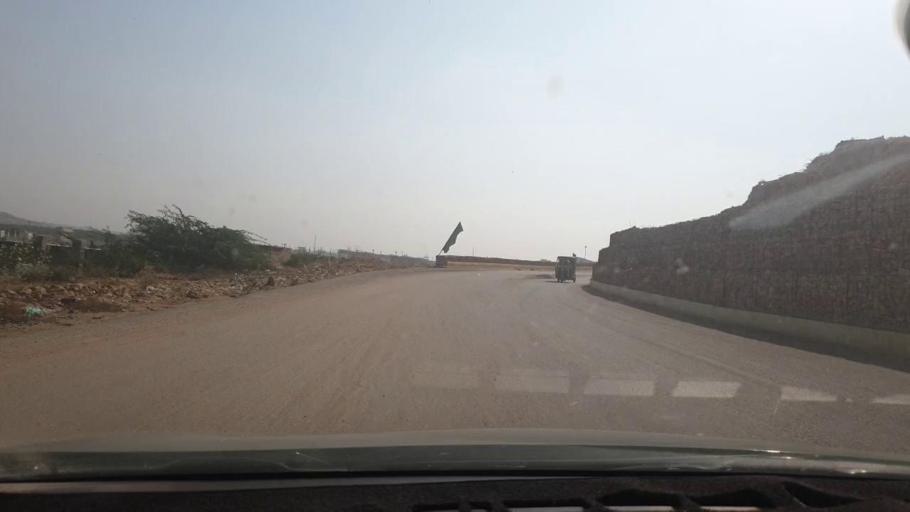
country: PK
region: Sindh
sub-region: Karachi District
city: Karachi
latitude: 24.9733
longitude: 66.9980
